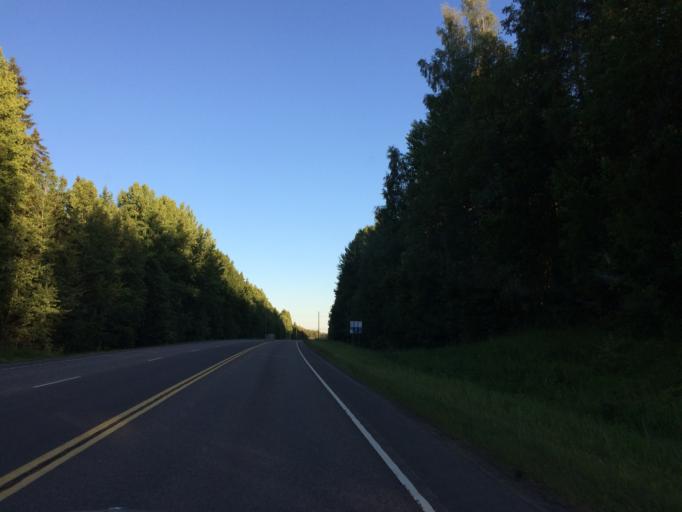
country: FI
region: Haeme
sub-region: Riihimaeki
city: Riihimaeki
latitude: 60.7620
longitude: 24.7149
